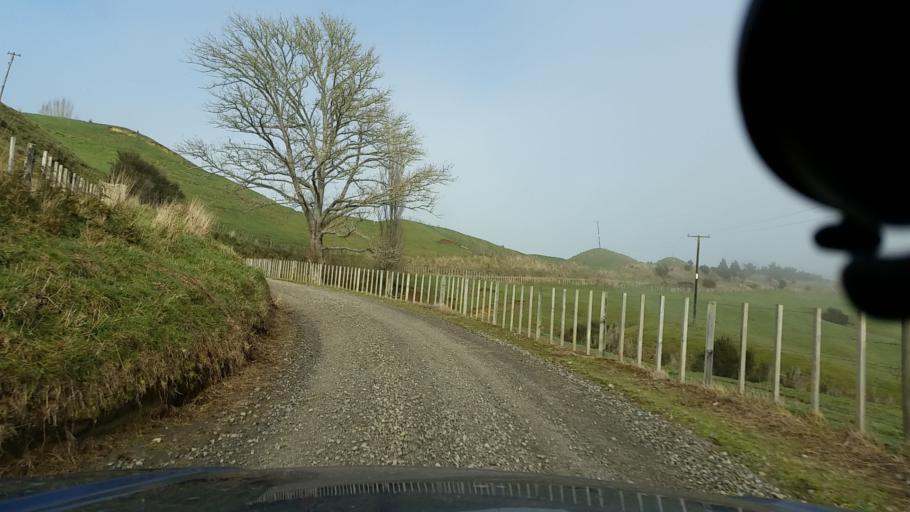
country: NZ
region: Taranaki
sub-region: New Plymouth District
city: Waitara
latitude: -38.9968
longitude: 174.7721
